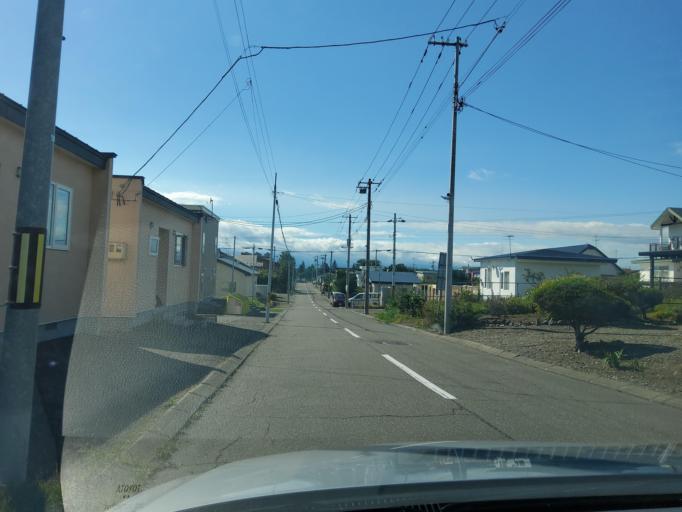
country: JP
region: Hokkaido
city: Obihiro
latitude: 42.9528
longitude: 143.1916
